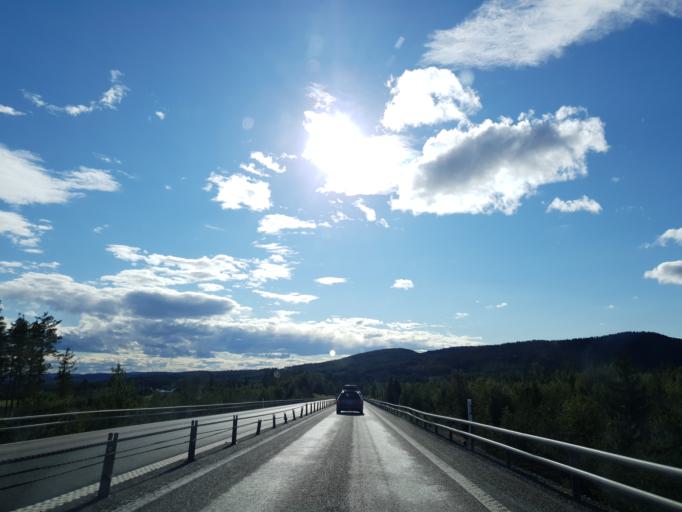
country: SE
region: Vaesternorrland
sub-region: Kramfors Kommun
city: Nordingra
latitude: 62.8774
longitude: 18.0706
